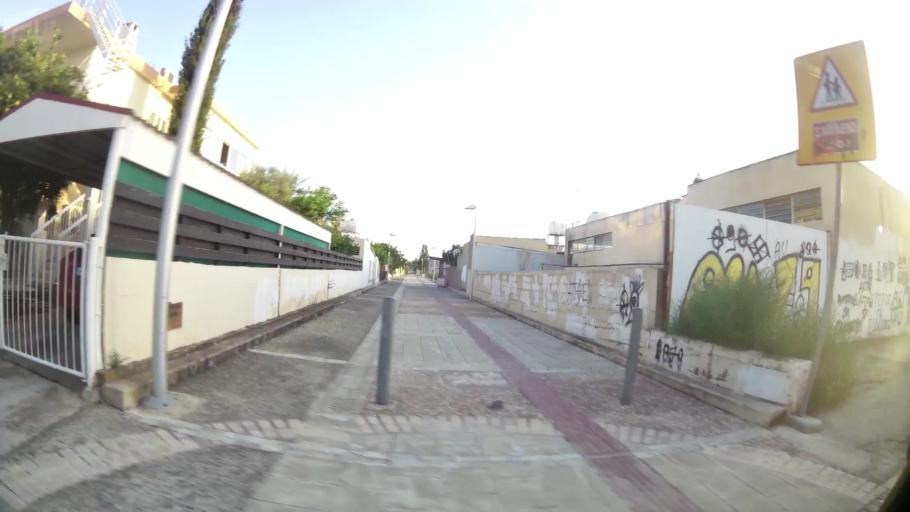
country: CY
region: Lefkosia
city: Nicosia
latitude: 35.1706
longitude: 33.3220
